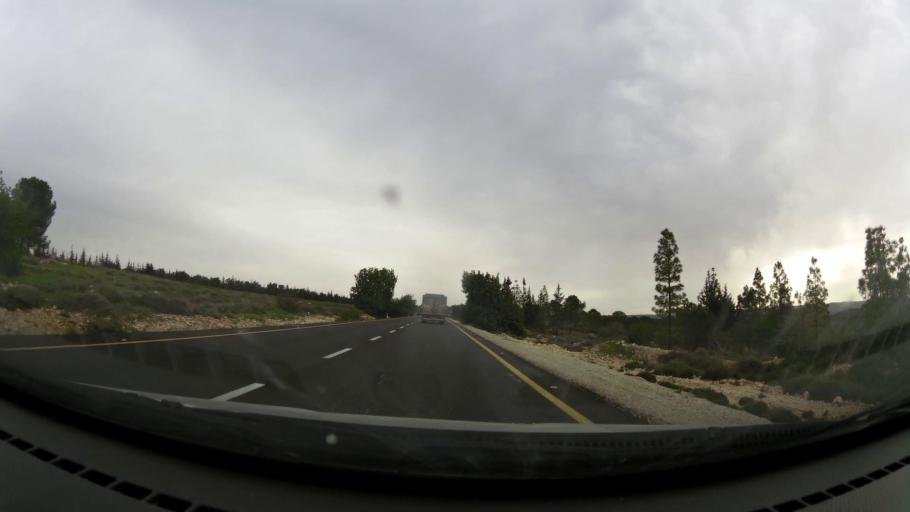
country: PS
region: West Bank
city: Surif
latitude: 31.6755
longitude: 35.0373
